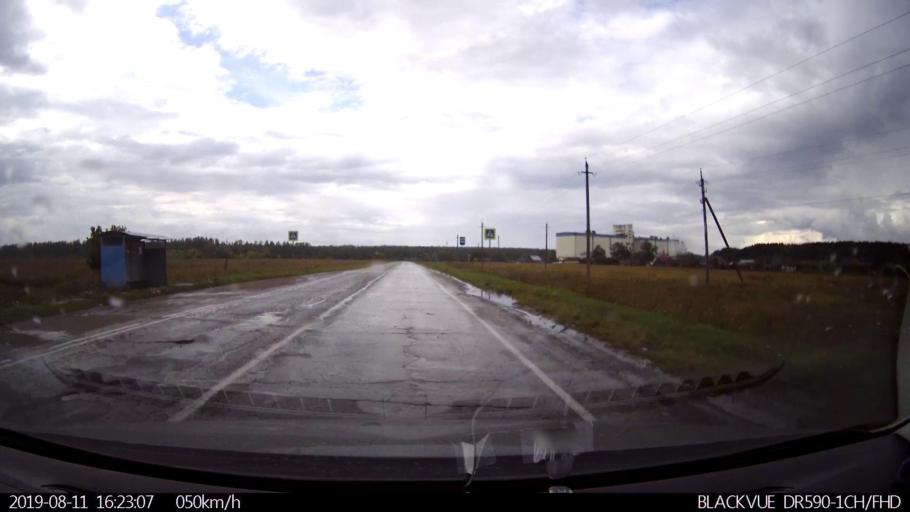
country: RU
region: Ulyanovsk
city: Mayna
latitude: 54.0929
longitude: 47.5899
